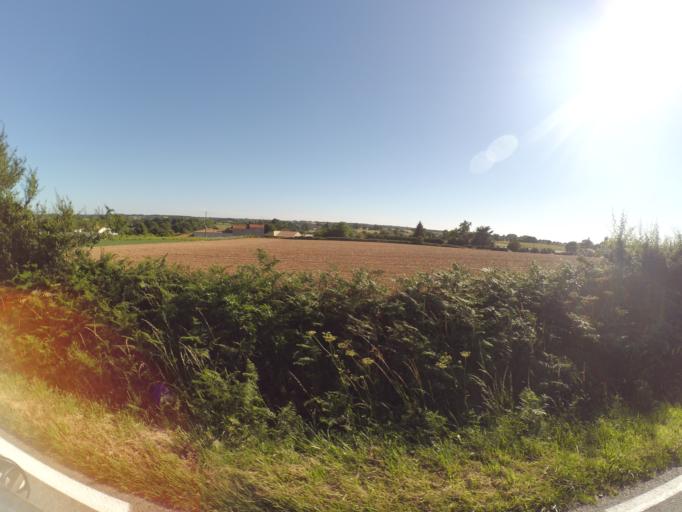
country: FR
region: Pays de la Loire
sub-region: Departement de la Vendee
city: Saint-Paul-en-Pareds
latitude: 46.8596
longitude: -0.9668
